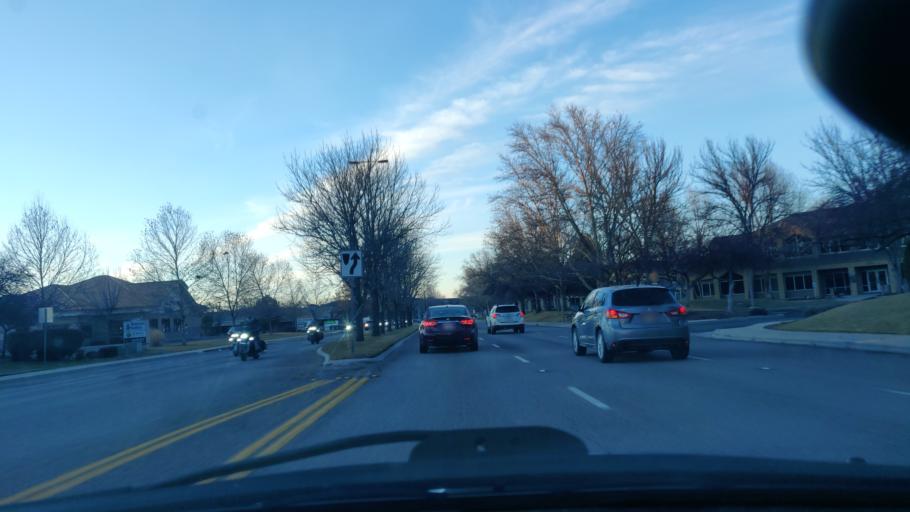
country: US
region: Idaho
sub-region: Ada County
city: Boise
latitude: 43.5898
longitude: -116.1748
